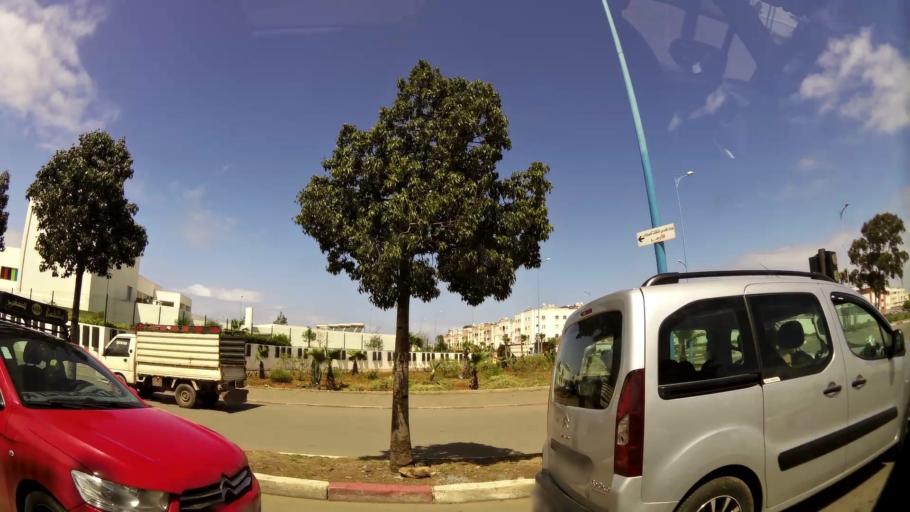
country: MA
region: Grand Casablanca
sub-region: Mediouna
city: Tit Mellil
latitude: 33.5975
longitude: -7.4937
